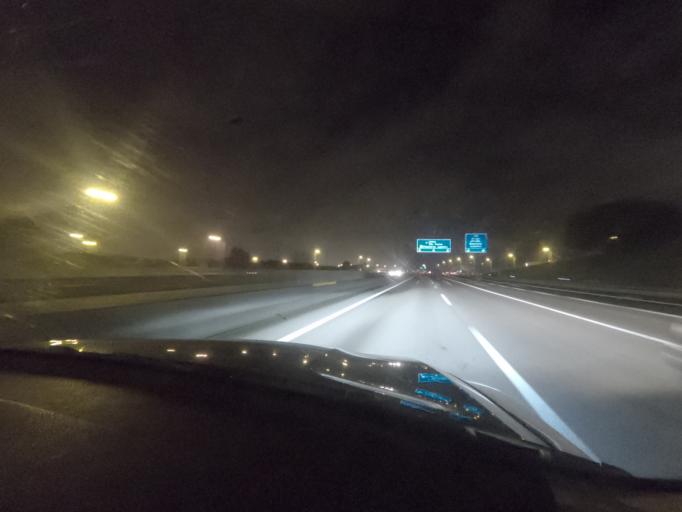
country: PT
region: Lisbon
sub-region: Alenquer
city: Carregado
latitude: 39.0245
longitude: -8.9633
